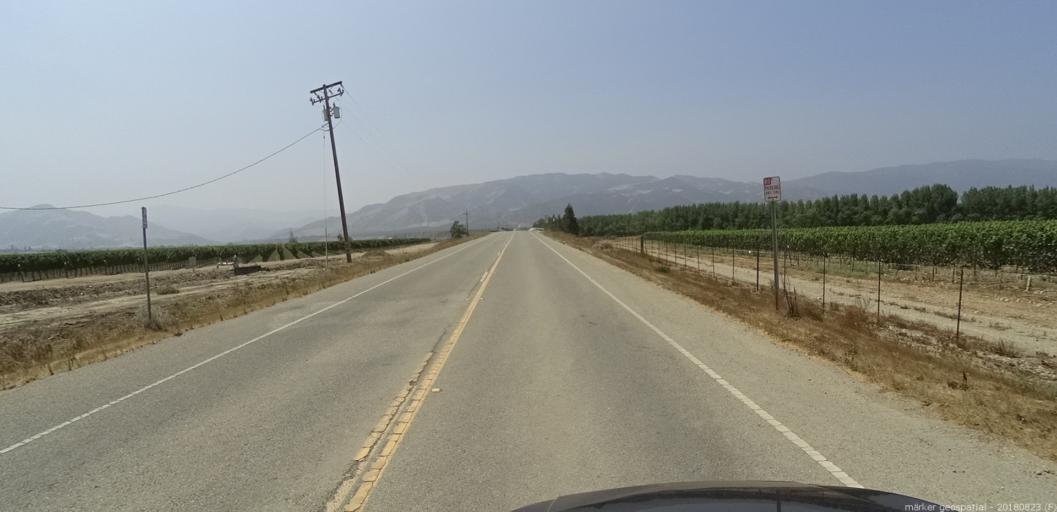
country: US
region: California
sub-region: Monterey County
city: Greenfield
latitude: 36.3241
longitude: -121.2902
